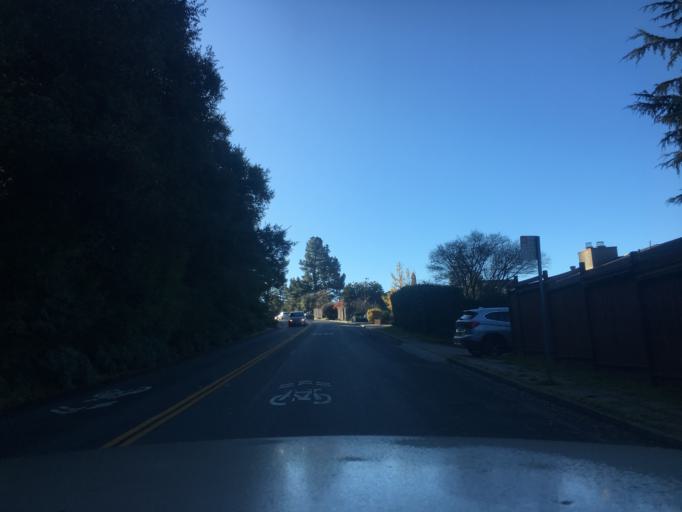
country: US
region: California
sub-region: Alameda County
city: Berkeley
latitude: 37.8887
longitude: -122.2519
